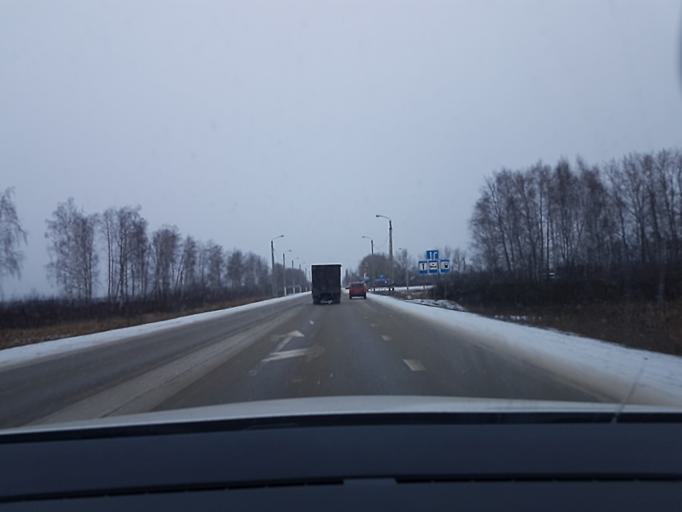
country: RU
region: Tambov
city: Pervomayskiy
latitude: 53.2441
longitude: 40.2557
